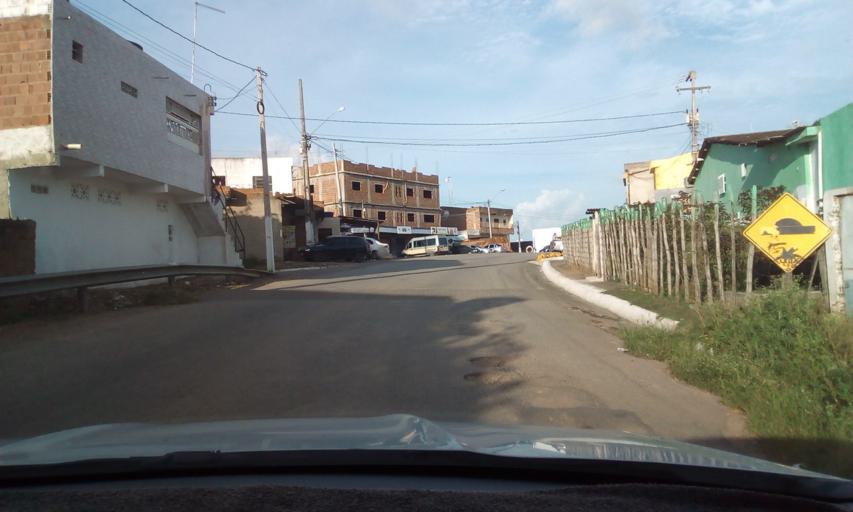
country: BR
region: Pernambuco
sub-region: Gloria Do Goita
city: Gloria do Goita
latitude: -7.9951
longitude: -35.2132
